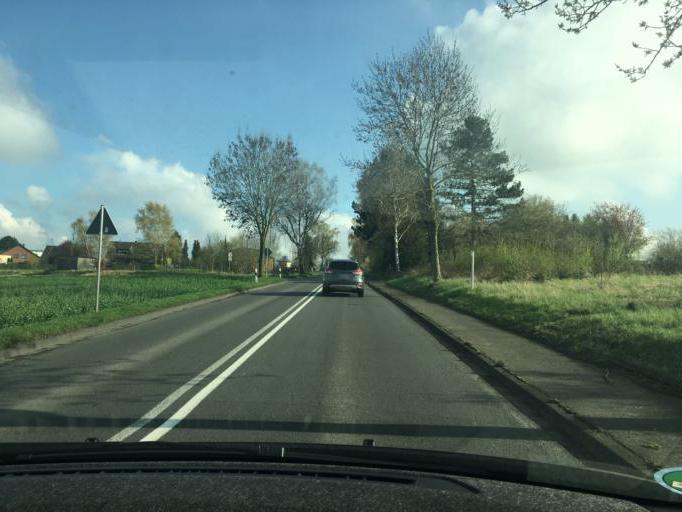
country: DE
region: North Rhine-Westphalia
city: Bornheim
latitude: 50.7548
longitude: 6.9631
